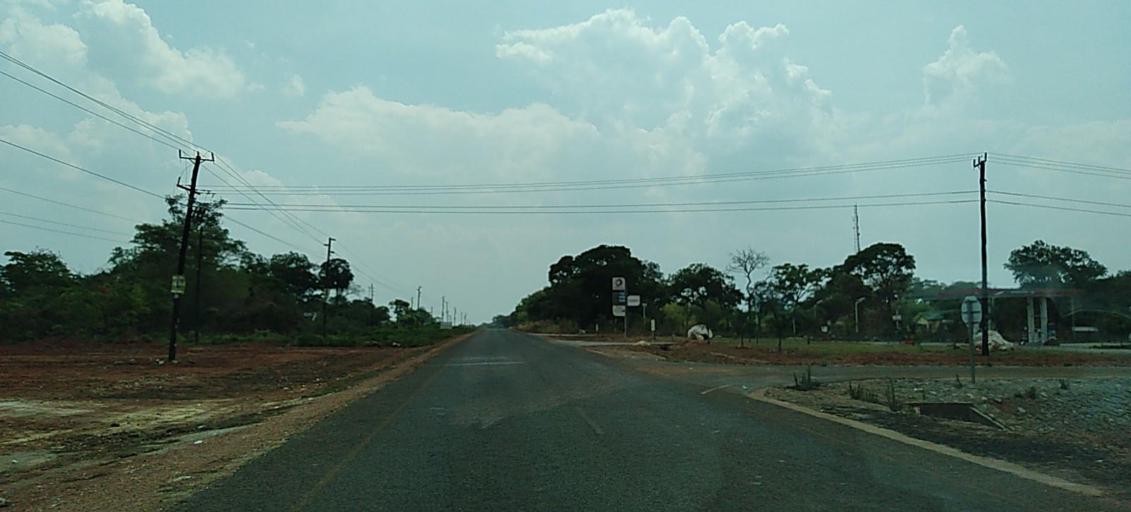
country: ZM
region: Copperbelt
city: Chingola
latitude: -12.8571
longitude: 27.6301
